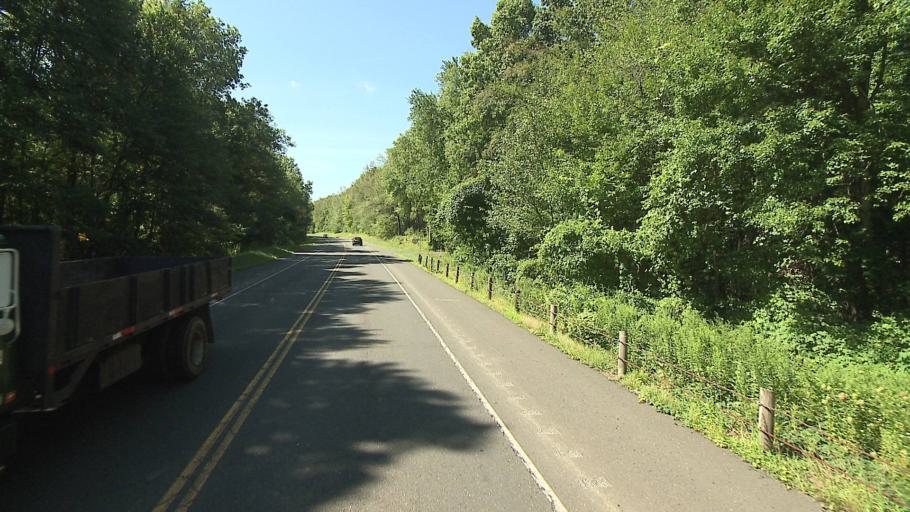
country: US
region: Connecticut
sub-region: Hartford County
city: Tariffville
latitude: 41.9119
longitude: -72.7458
